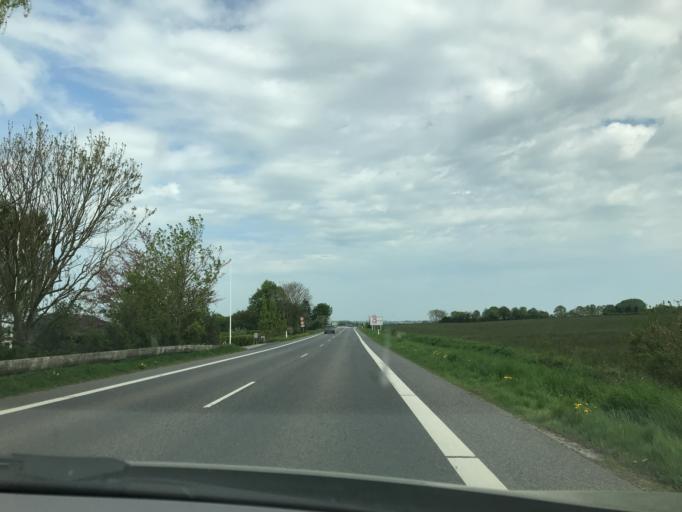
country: DK
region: South Denmark
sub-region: Assens Kommune
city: Assens
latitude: 55.2932
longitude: 9.9350
